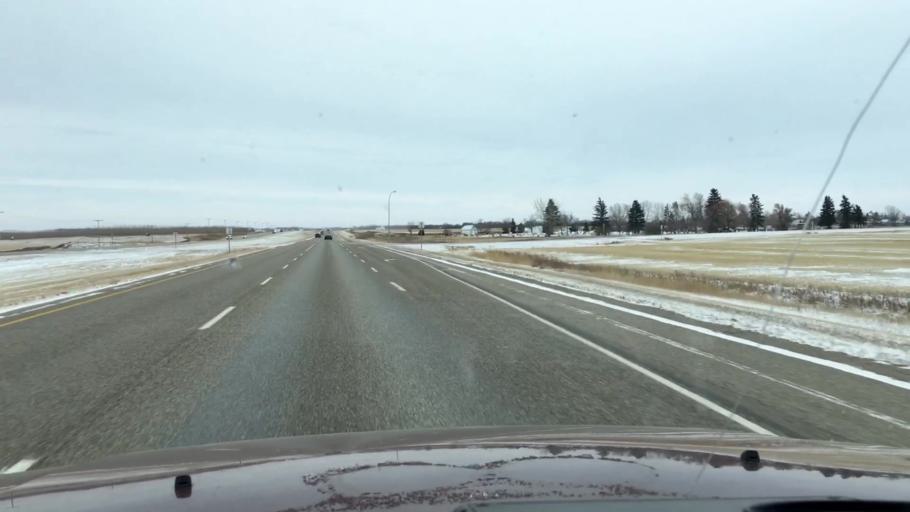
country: CA
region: Saskatchewan
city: Watrous
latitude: 51.0612
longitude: -105.8240
